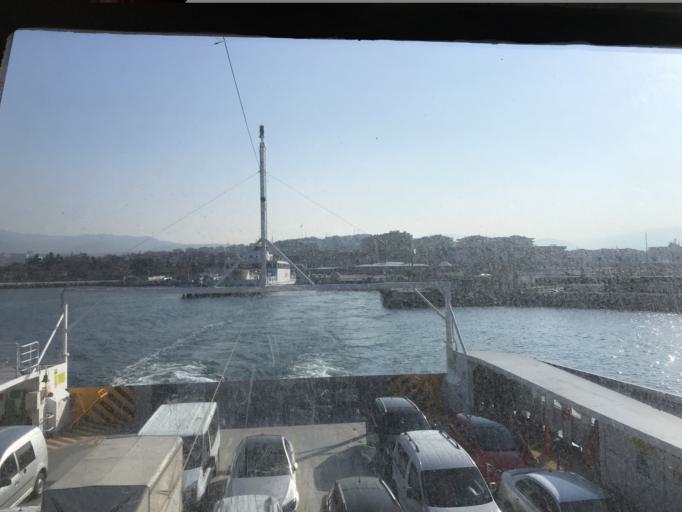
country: TR
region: Yalova
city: Yalova
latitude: 40.6627
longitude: 29.2790
